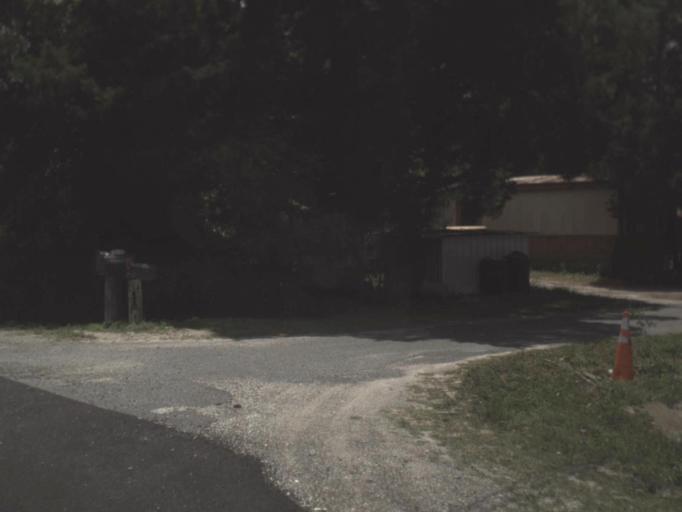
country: US
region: Florida
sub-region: Nassau County
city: Nassau Village-Ratliff
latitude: 30.4303
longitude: -81.7588
